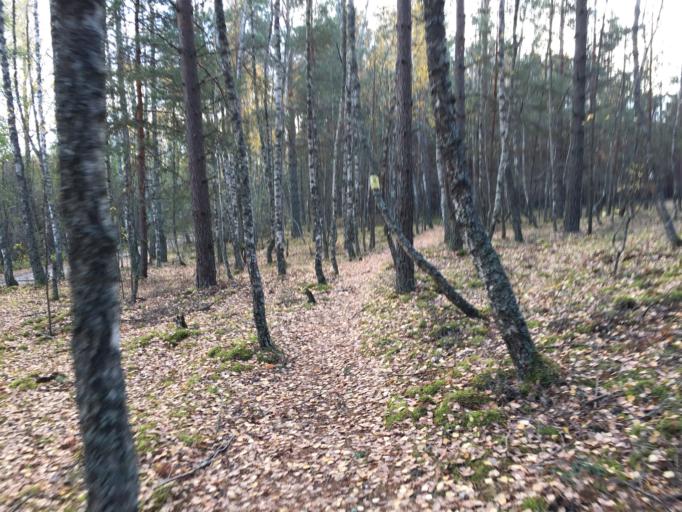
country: LV
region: Carnikava
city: Carnikava
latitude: 57.1473
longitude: 24.2633
